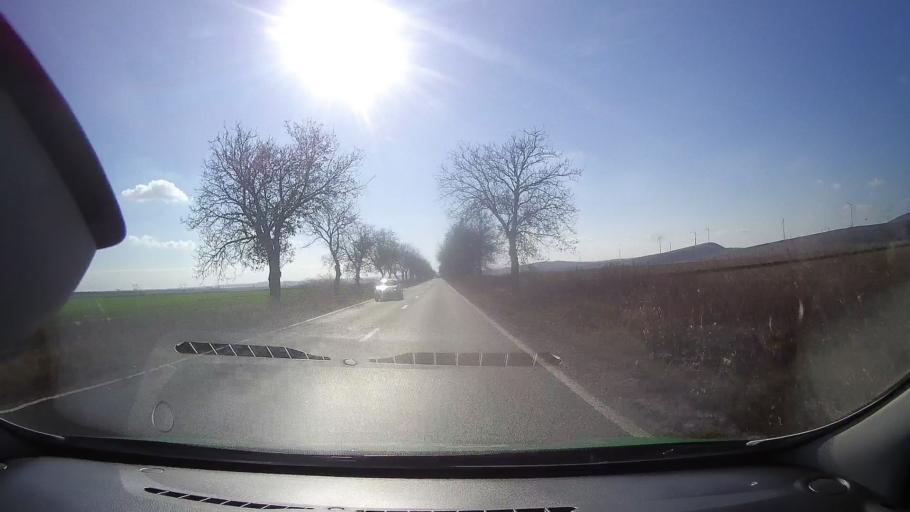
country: RO
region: Tulcea
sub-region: Comuna Ceamurlia de Jos
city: Ceamurlia de Jos
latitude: 44.7926
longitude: 28.6900
